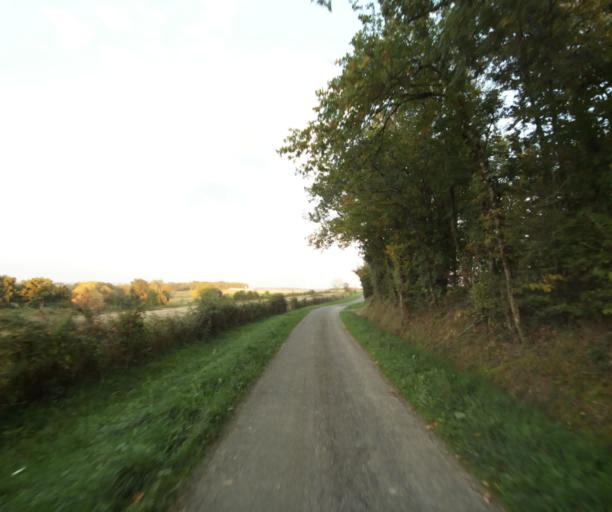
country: FR
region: Midi-Pyrenees
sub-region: Departement du Gers
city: Vic-Fezensac
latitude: 43.7869
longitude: 0.2255
